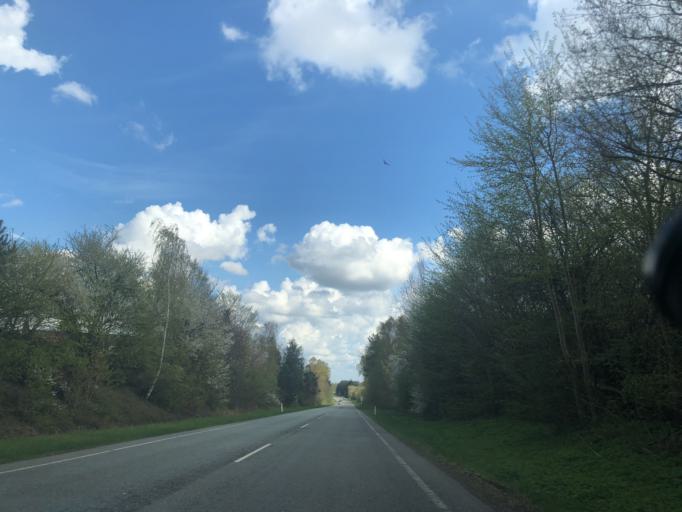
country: DK
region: Capital Region
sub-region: Gribskov Kommune
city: Helsinge
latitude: 56.0152
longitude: 12.1891
